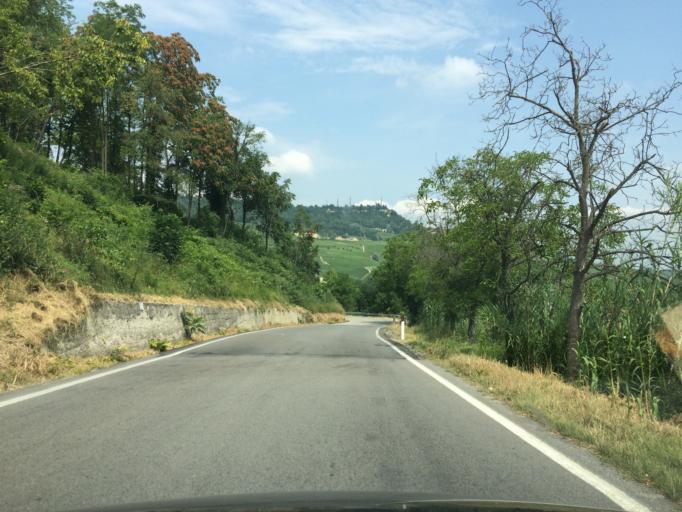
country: IT
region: Piedmont
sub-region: Provincia di Cuneo
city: Barolo
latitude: 44.6143
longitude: 7.9373
